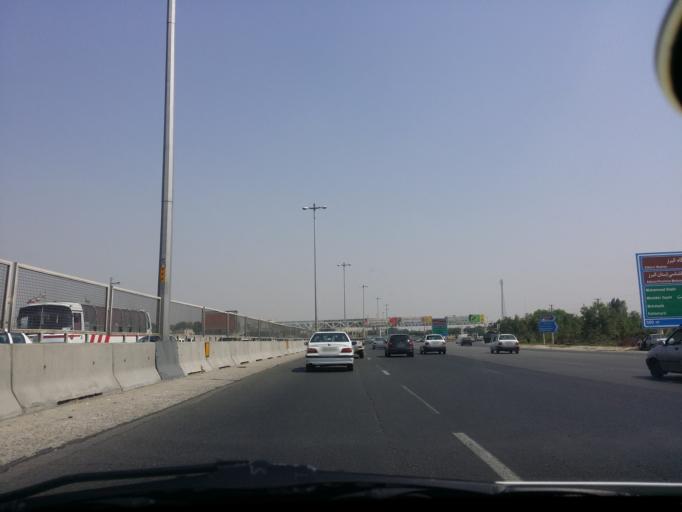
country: IR
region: Alborz
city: Karaj
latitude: 35.8046
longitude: 50.9676
